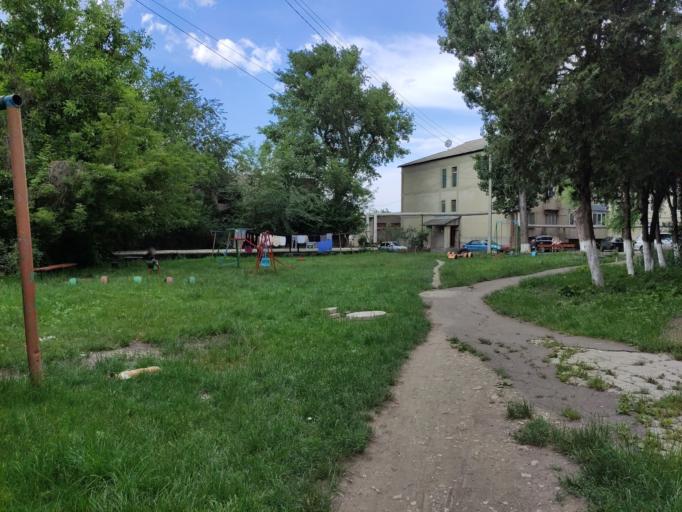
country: MD
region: Balti
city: Balti
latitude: 47.7546
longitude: 27.9365
